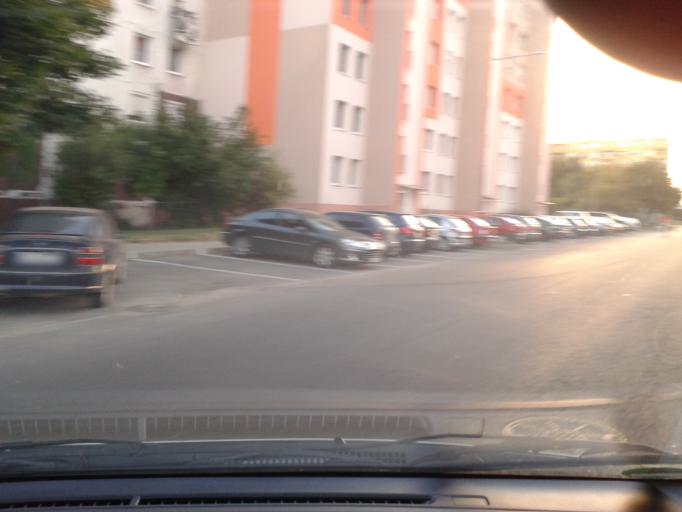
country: SK
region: Nitriansky
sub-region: Okres Nove Zamky
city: Sturovo
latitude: 47.7918
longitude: 18.7214
